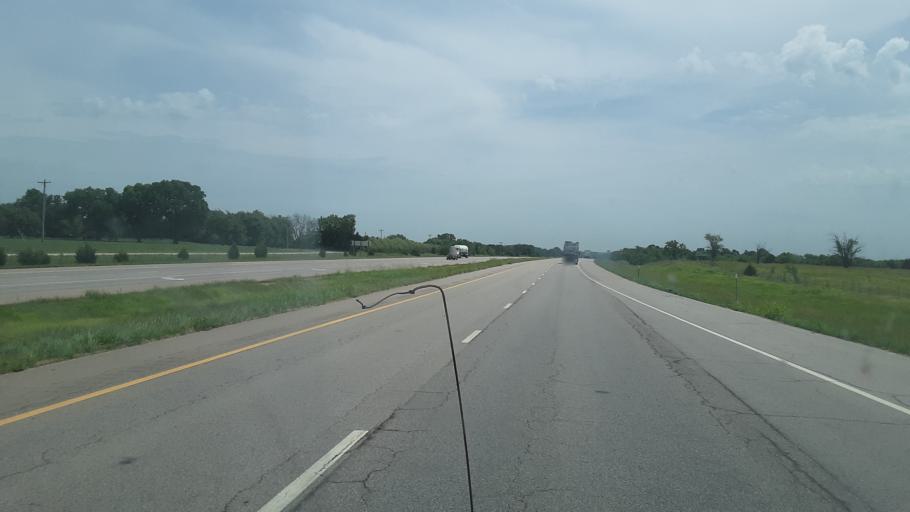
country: US
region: Kansas
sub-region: Butler County
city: Towanda
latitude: 37.7957
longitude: -97.0340
